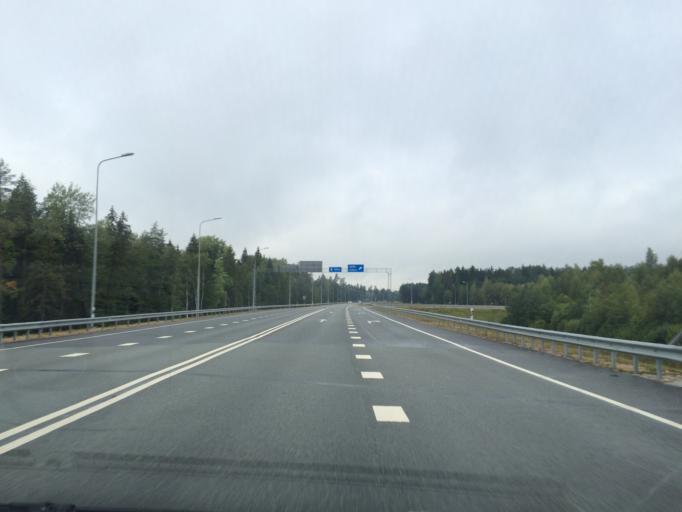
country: LV
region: Ogre
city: Ogre
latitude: 56.8443
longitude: 24.6741
